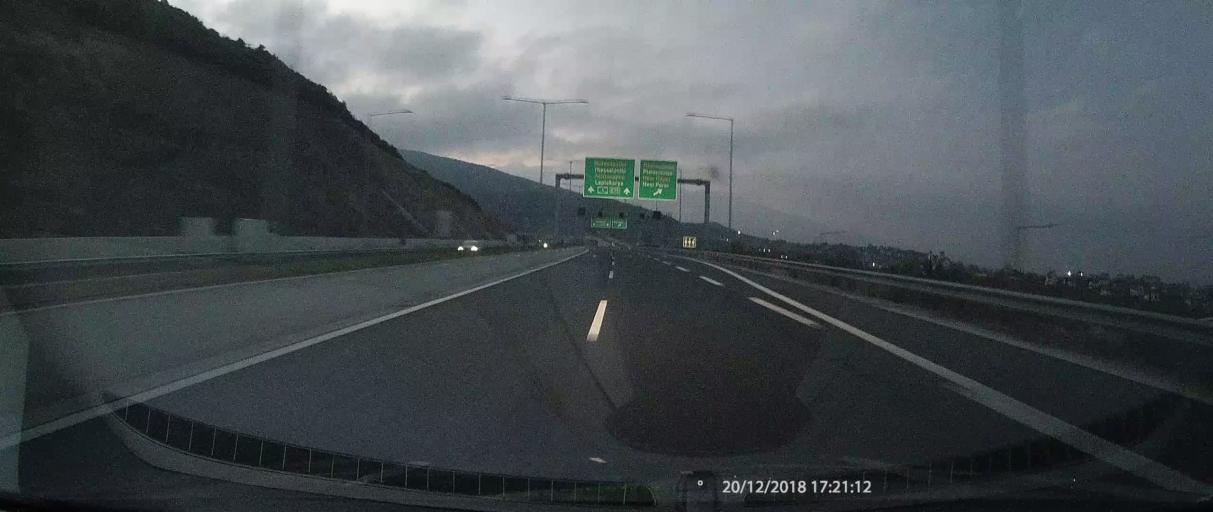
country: GR
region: Thessaly
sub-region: Nomos Larisis
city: Pyrgetos
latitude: 39.9772
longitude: 22.6327
